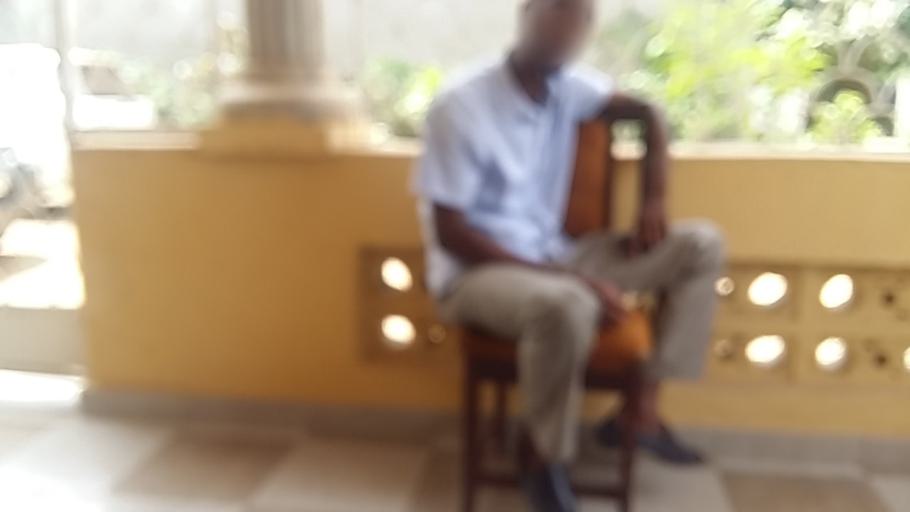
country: CD
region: Eastern Province
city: Kisangani
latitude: 0.5344
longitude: 25.2041
